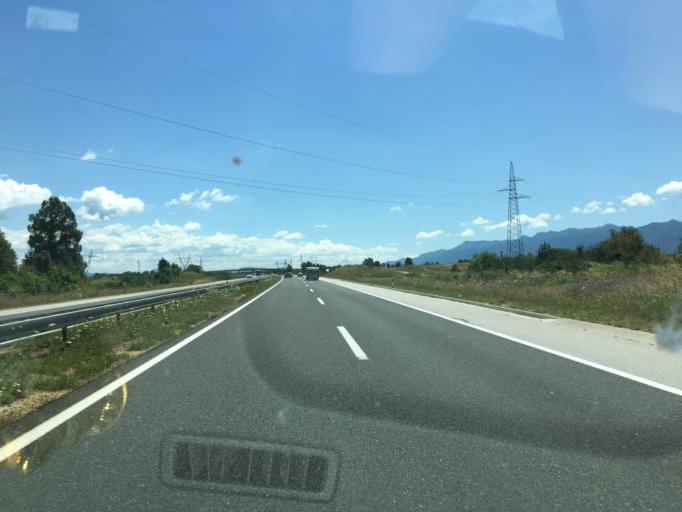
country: HR
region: Licko-Senjska
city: Gospic
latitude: 44.5317
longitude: 15.4464
